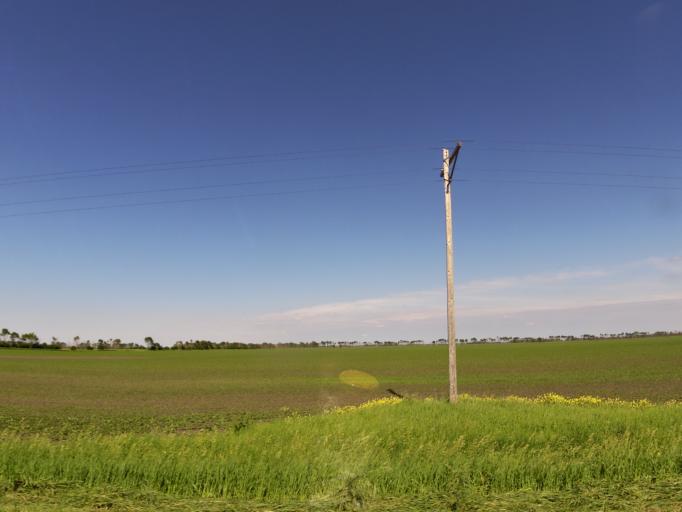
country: US
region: North Dakota
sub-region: Walsh County
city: Grafton
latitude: 48.3154
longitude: -97.2552
